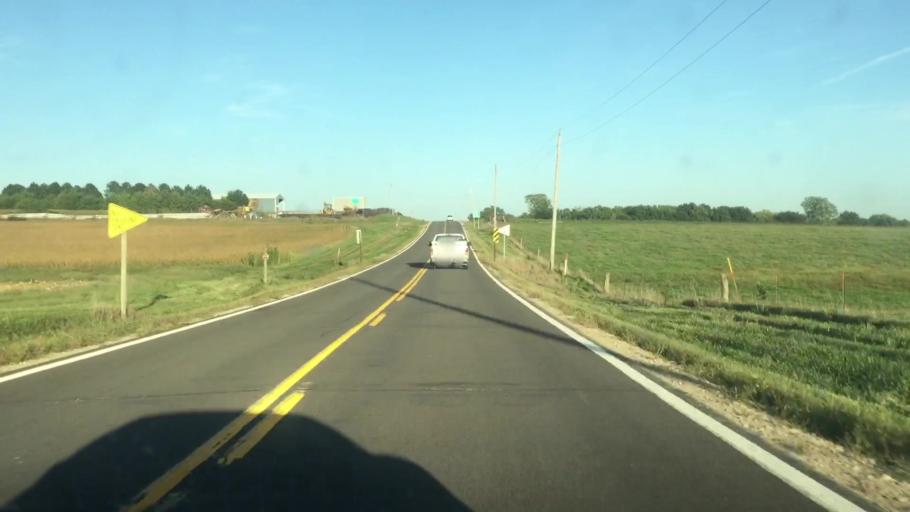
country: US
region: Kansas
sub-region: Brown County
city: Horton
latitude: 39.5512
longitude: -95.4135
